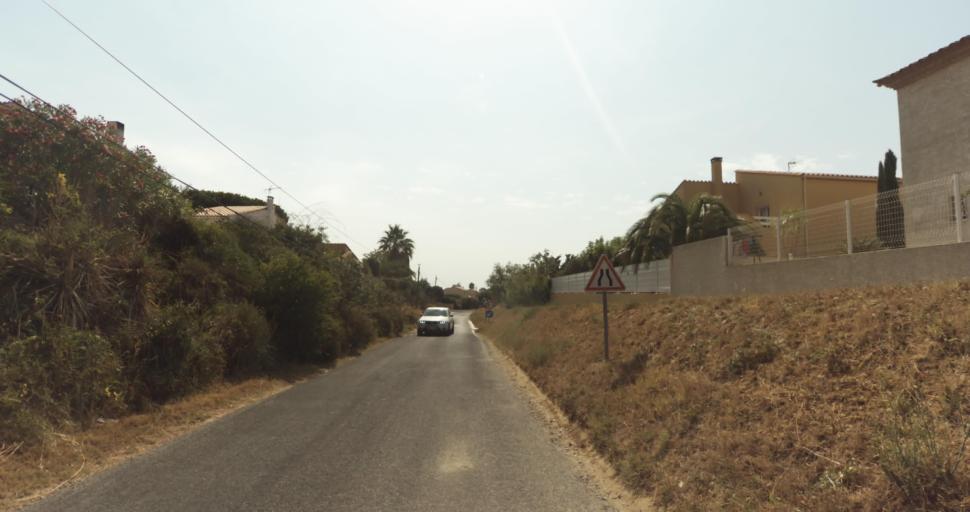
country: FR
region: Languedoc-Roussillon
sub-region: Departement des Pyrenees-Orientales
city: Latour-Bas-Elne
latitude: 42.6150
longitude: 3.0102
